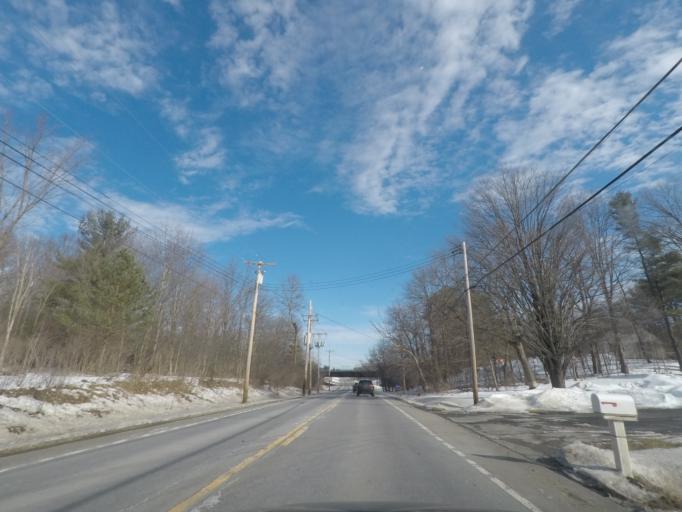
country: US
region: New York
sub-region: Albany County
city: Altamont
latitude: 42.7782
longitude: -74.0502
